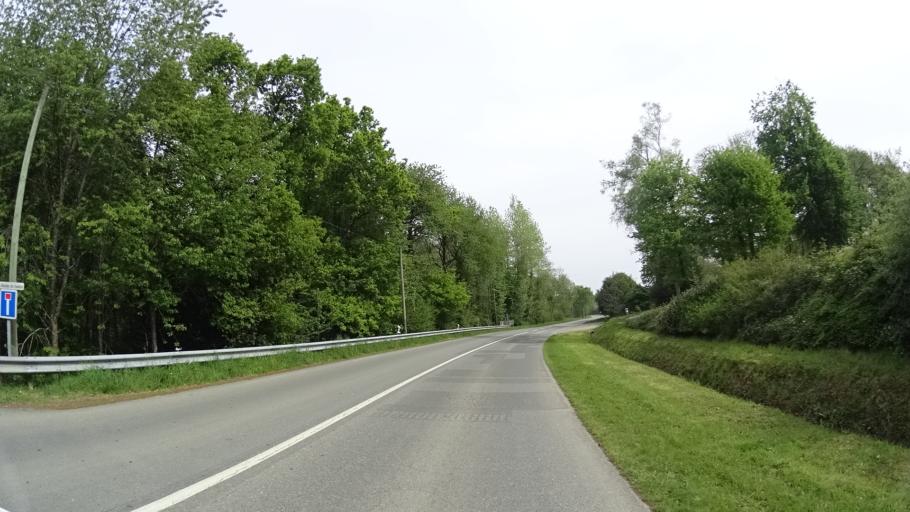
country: FR
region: Brittany
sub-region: Departement d'Ille-et-Vilaine
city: Vignoc
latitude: 48.2534
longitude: -1.7791
